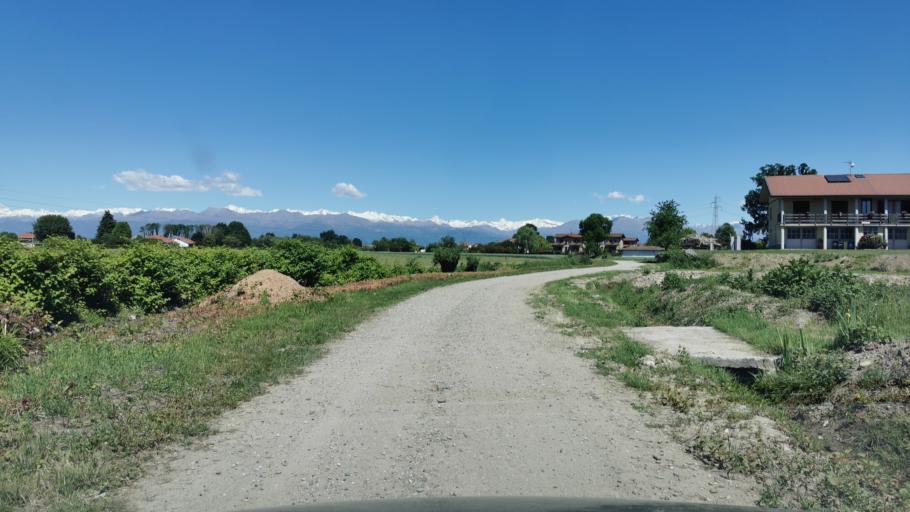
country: IT
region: Piedmont
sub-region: Provincia di Torino
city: Leini
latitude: 45.1673
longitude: 7.7259
